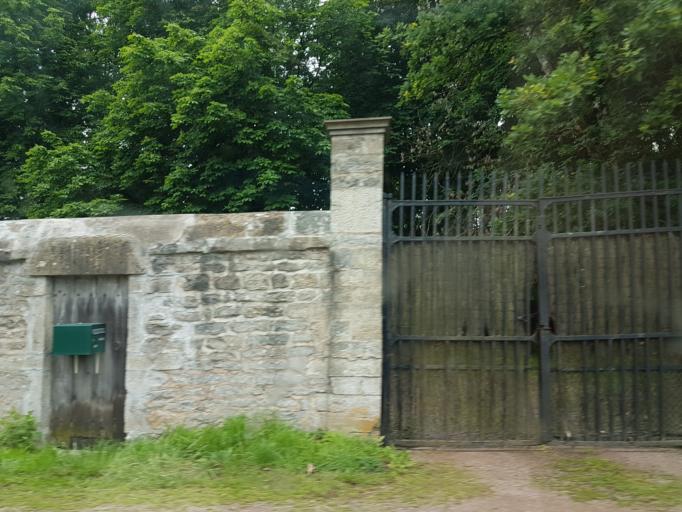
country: FR
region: Bourgogne
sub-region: Departement de la Nievre
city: Corbigny
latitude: 47.2165
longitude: 3.7017
